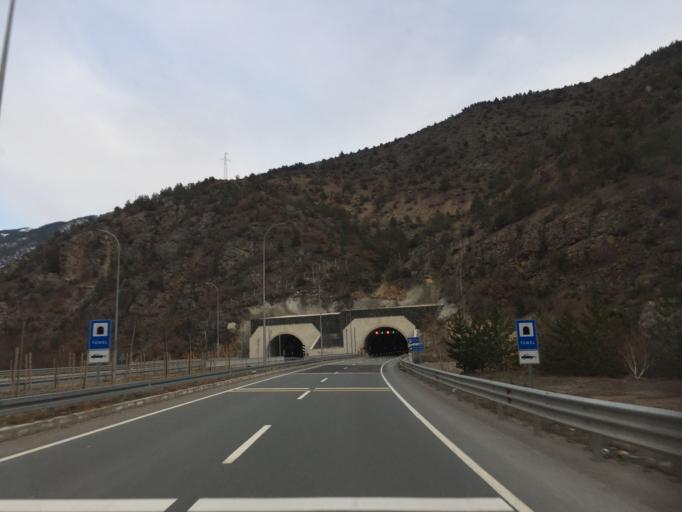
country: TR
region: Gumushane
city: Gumushkhane
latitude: 40.5185
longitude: 39.4104
